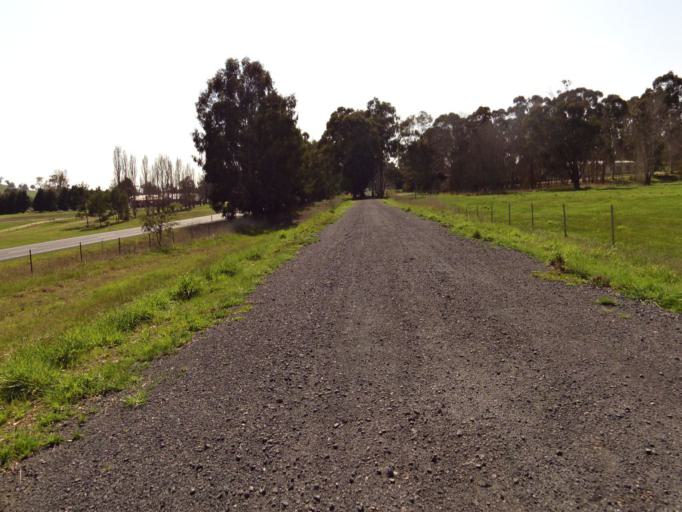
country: AU
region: Victoria
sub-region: Murrindindi
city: Alexandra
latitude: -37.1291
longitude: 145.5957
